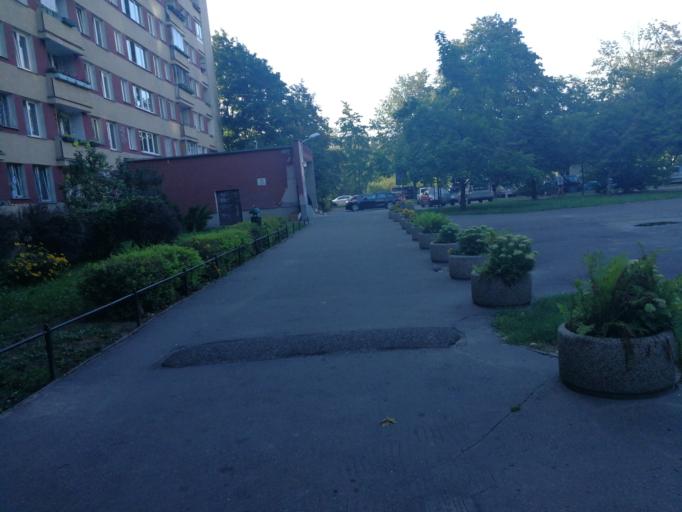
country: PL
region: Masovian Voivodeship
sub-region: Warszawa
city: Targowek
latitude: 52.2875
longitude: 21.0378
